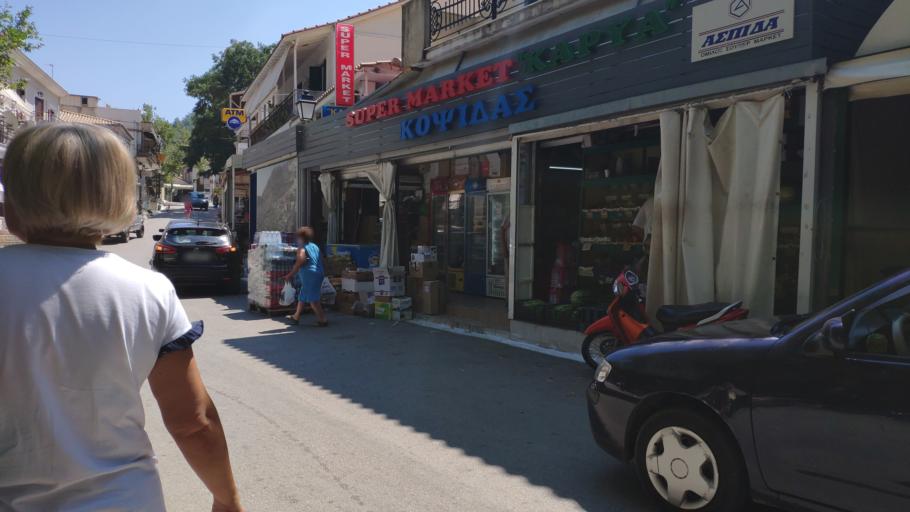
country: GR
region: Ionian Islands
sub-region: Lefkada
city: Nidri
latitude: 38.7598
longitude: 20.6485
